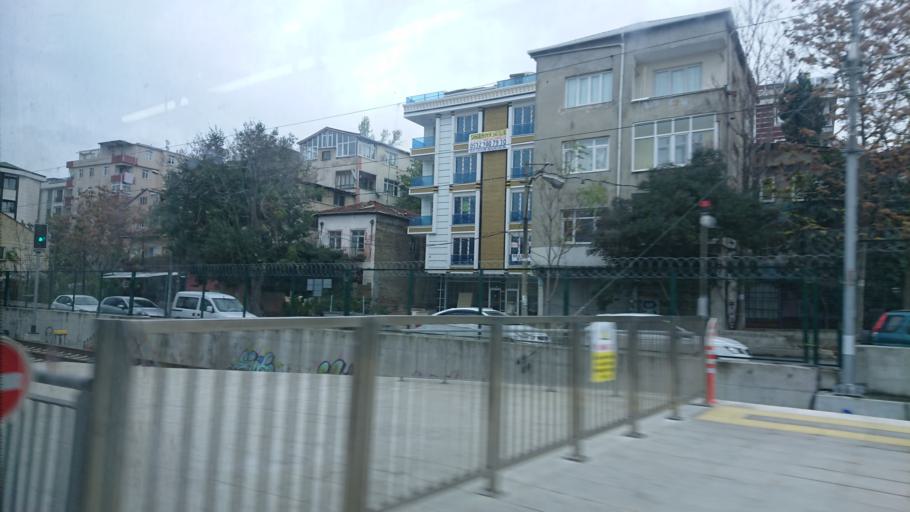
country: TR
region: Istanbul
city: Mahmutbey
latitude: 40.9896
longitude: 28.7727
